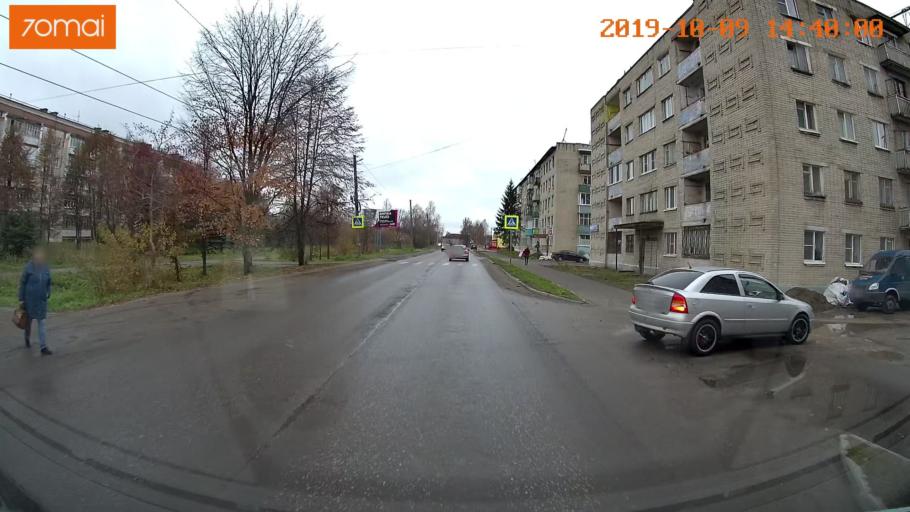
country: RU
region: Kostroma
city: Buy
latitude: 58.4763
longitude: 41.5367
